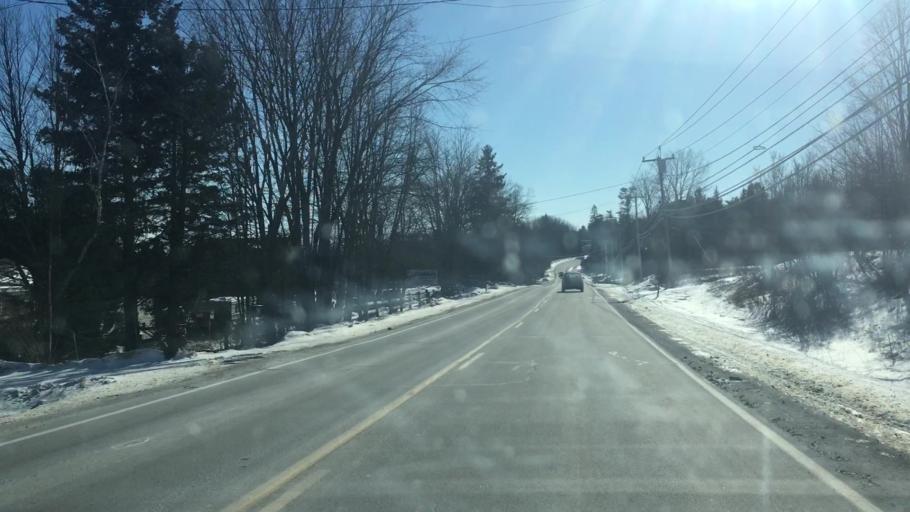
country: US
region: Maine
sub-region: Hancock County
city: Ellsworth
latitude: 44.5240
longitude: -68.4315
